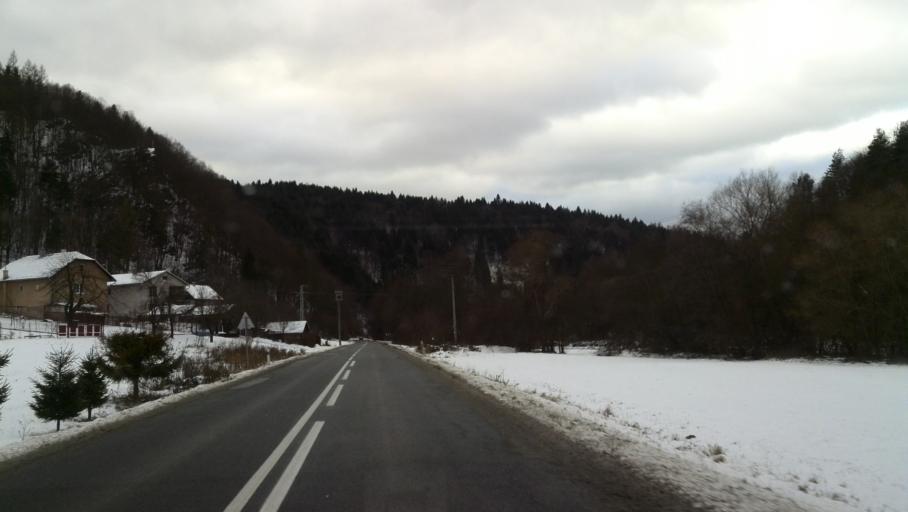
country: SK
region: Kosicky
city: Gelnica
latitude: 48.8711
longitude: 20.9778
